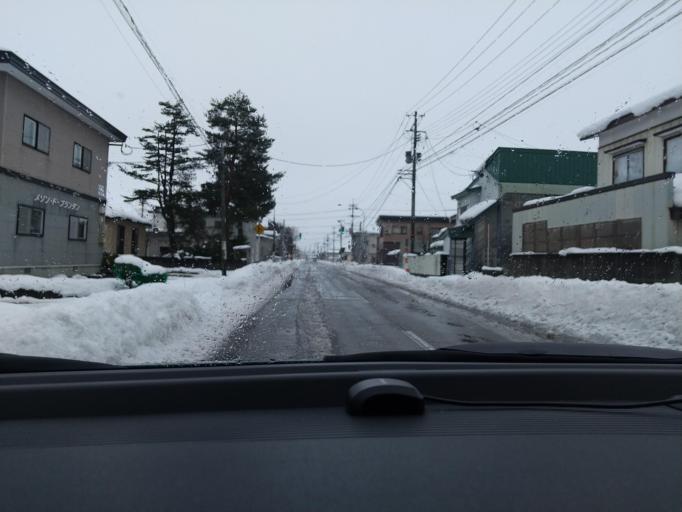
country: JP
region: Akita
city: Omagari
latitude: 39.4442
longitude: 140.4801
